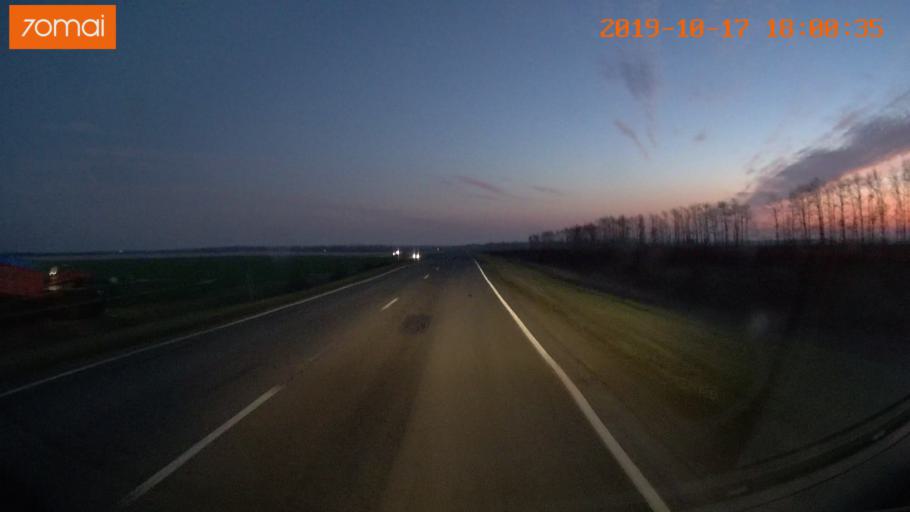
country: RU
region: Tula
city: Kurkino
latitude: 53.5200
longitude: 38.6141
